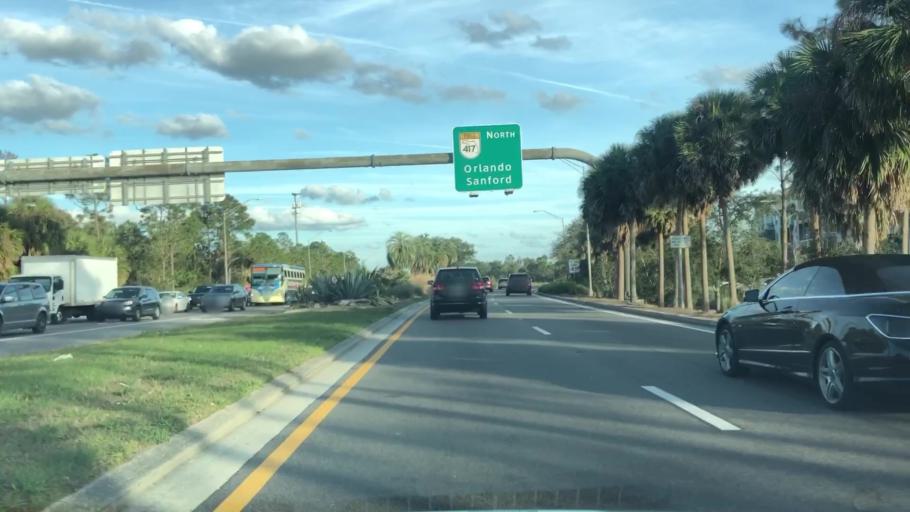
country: US
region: Florida
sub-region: Osceola County
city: Celebration
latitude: 28.3581
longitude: -81.4865
